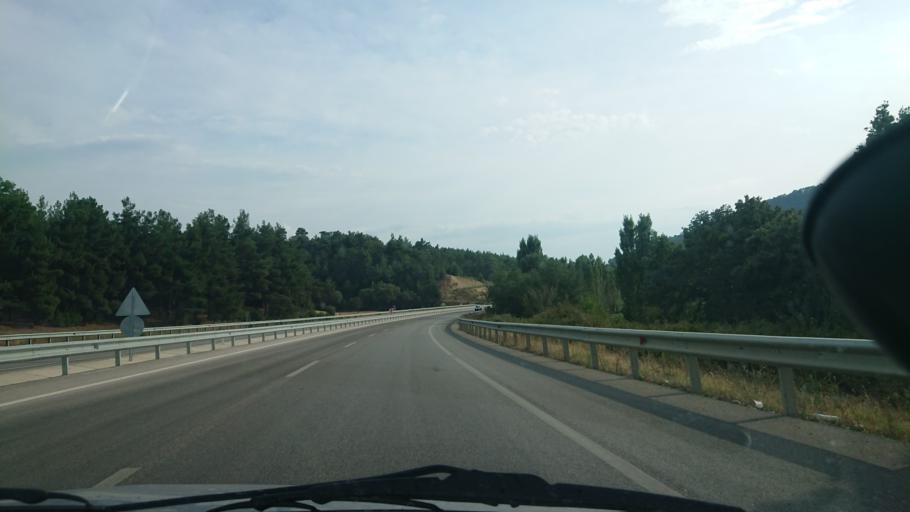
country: TR
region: Kuetahya
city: Gediz
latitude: 38.9173
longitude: 29.3020
